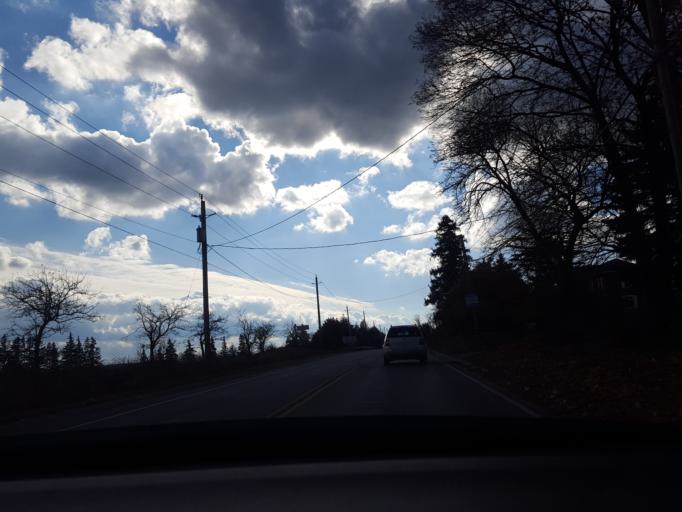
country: CA
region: Ontario
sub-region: Halton
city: Milton
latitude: 43.4762
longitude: -79.8952
